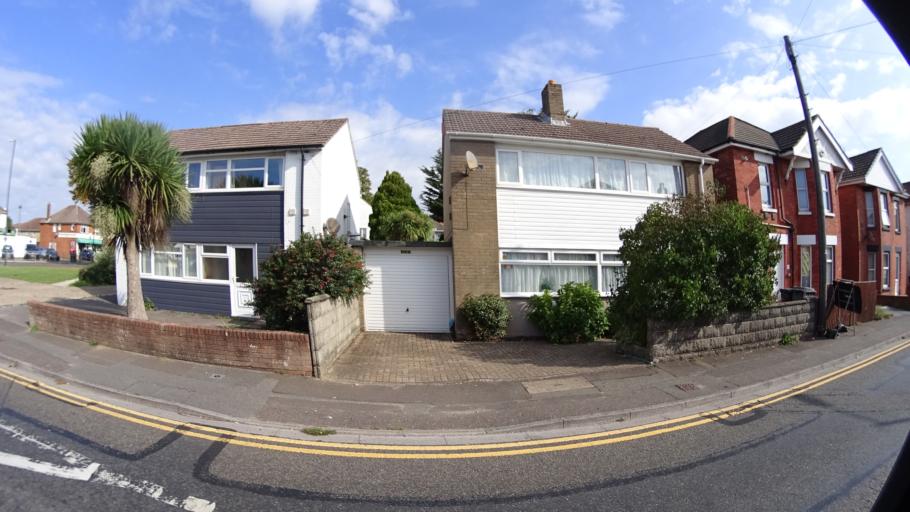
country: GB
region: England
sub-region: Bournemouth
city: Bournemouth
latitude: 50.7514
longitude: -1.8856
